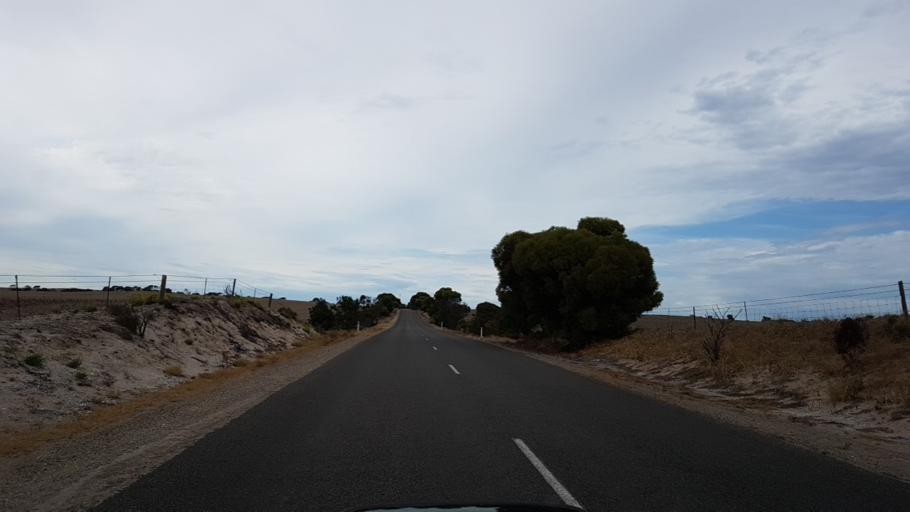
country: AU
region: South Australia
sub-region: Yorke Peninsula
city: Honiton
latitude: -34.9813
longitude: 137.1206
